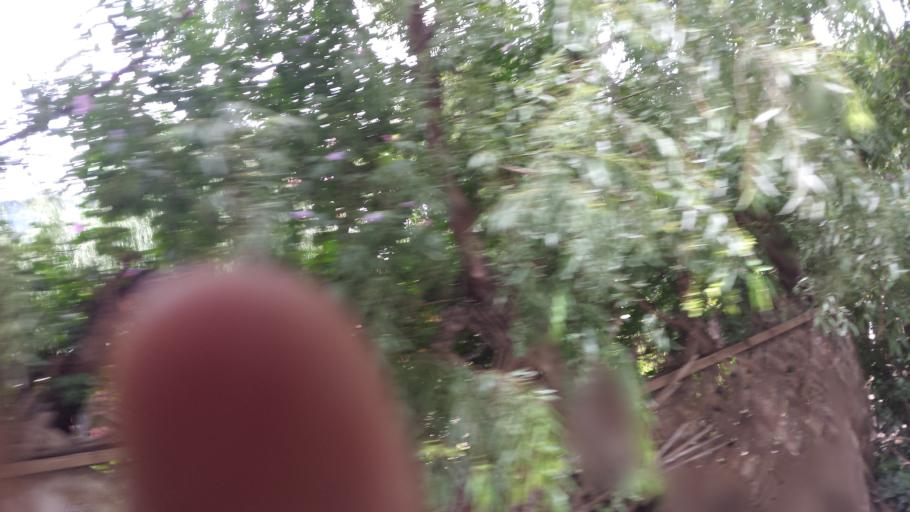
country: BT
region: Thimphu
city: Thimphu
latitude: 27.4738
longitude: 89.6281
